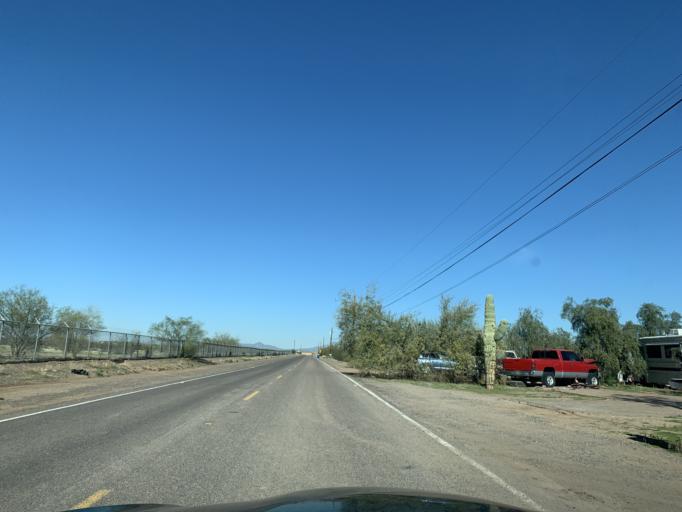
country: US
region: Arizona
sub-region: Maricopa County
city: Queen Creek
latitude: 33.3024
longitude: -111.6049
